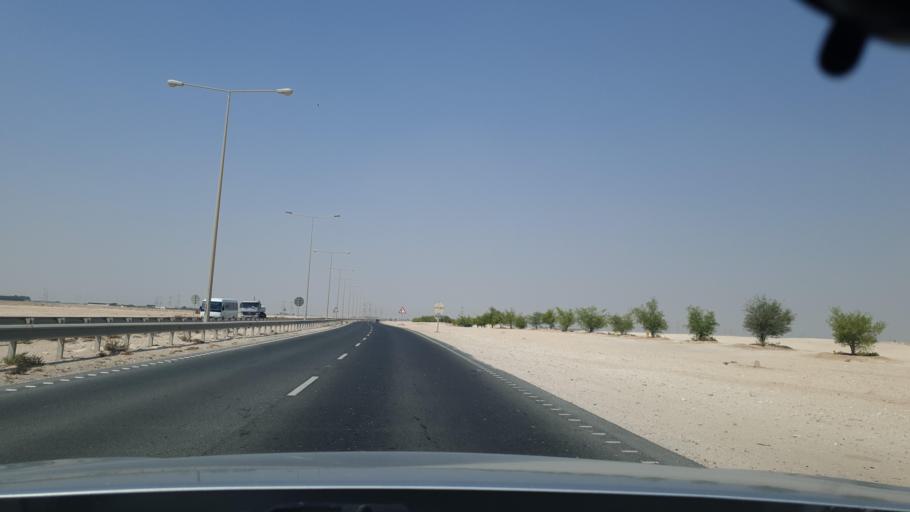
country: QA
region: Al Khawr
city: Al Khawr
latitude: 25.7383
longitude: 51.4897
